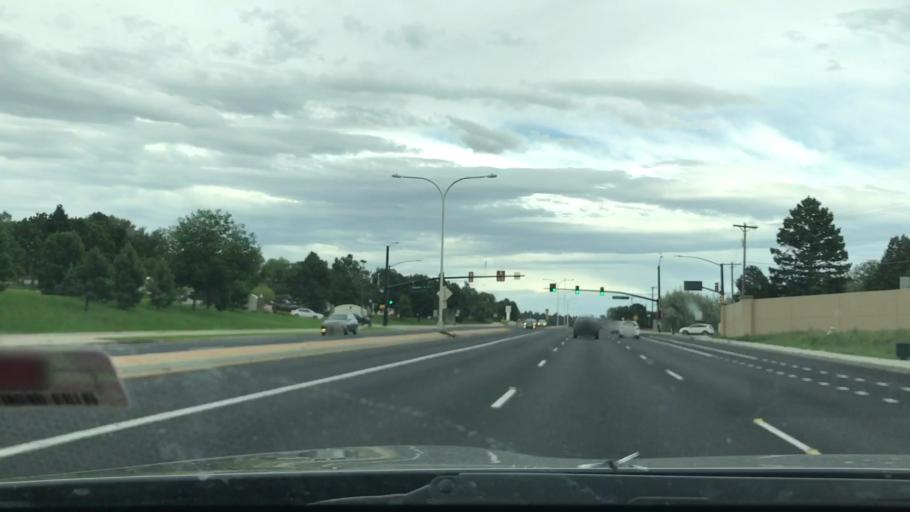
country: US
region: Colorado
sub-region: El Paso County
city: Colorado Springs
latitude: 38.8908
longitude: -104.7993
